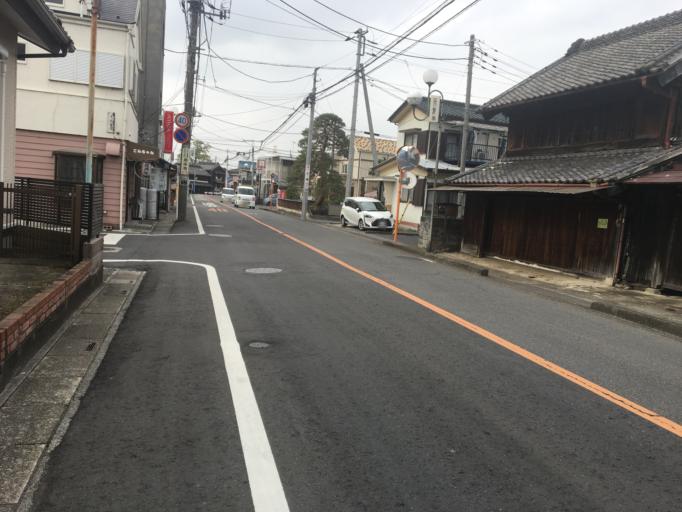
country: JP
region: Saitama
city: Sugito
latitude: 36.0299
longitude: 139.7265
